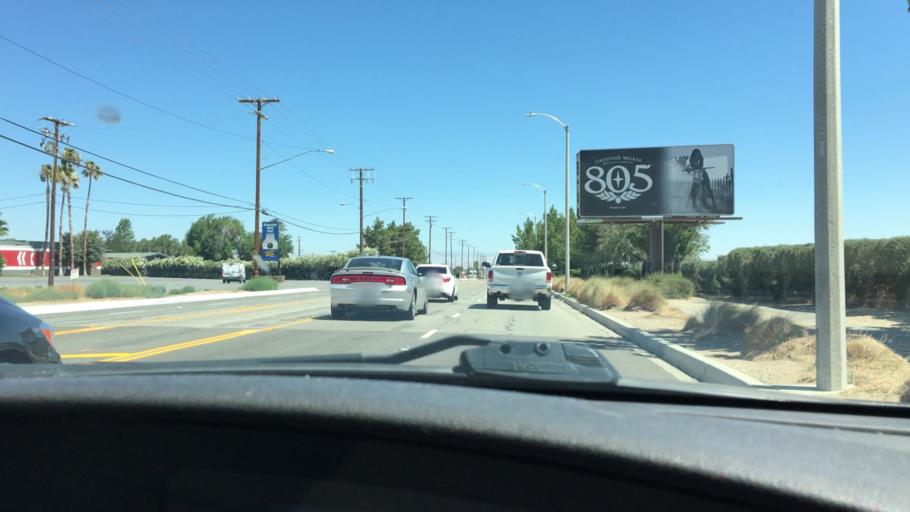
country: US
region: California
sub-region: Los Angeles County
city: Lancaster
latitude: 34.6680
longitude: -118.1317
